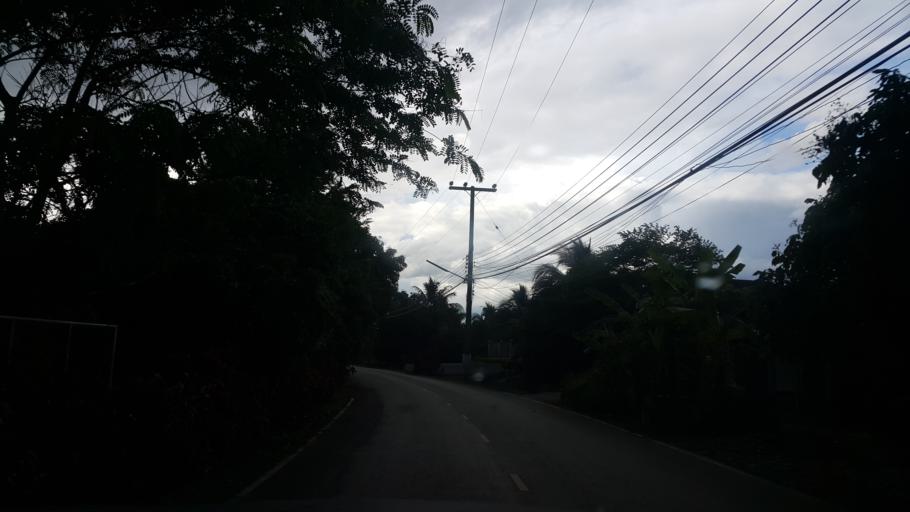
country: TH
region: Chiang Mai
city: Mae Taeng
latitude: 19.0778
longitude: 98.9520
